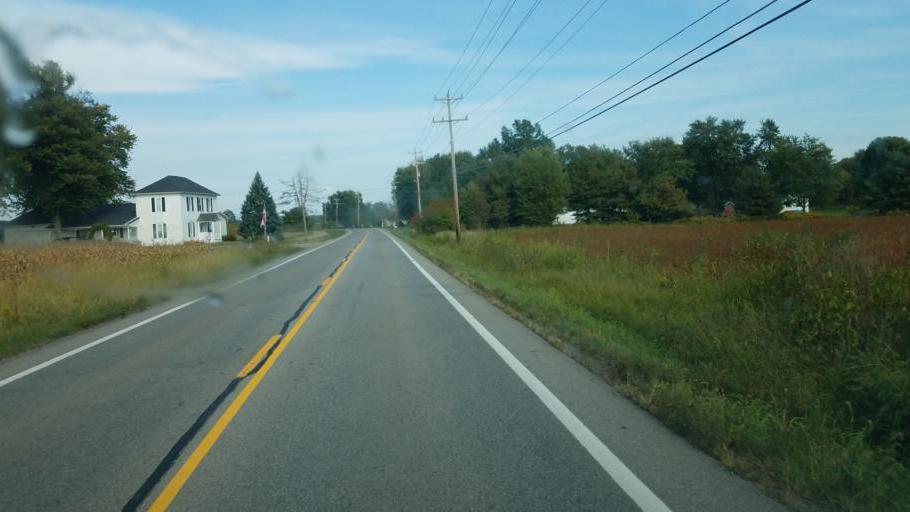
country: US
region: Ohio
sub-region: Franklin County
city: New Albany
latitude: 40.1219
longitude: -82.7582
